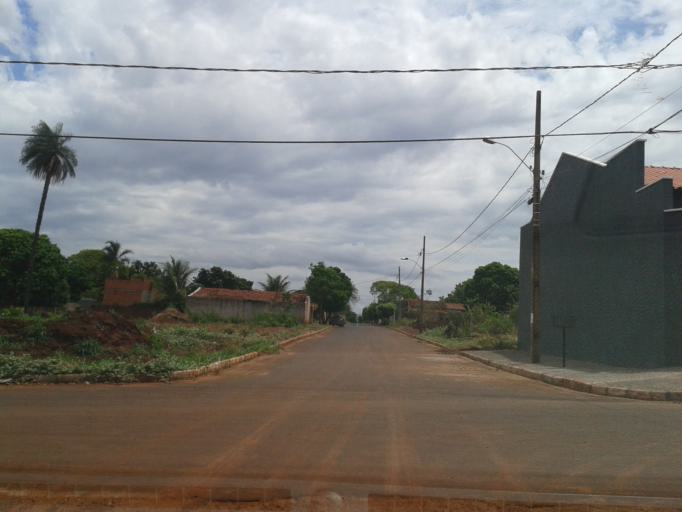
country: BR
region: Minas Gerais
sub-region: Ituiutaba
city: Ituiutaba
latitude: -18.9969
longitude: -49.4609
